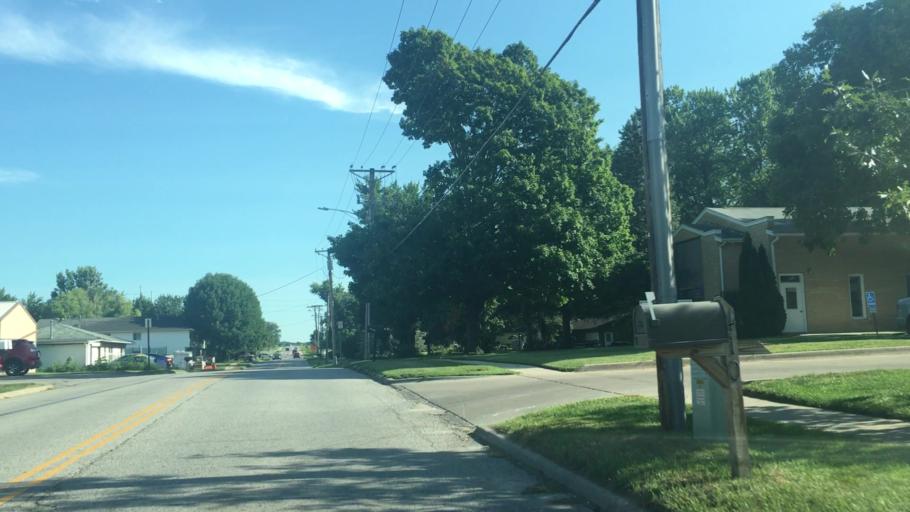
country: US
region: Iowa
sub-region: Johnson County
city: North Liberty
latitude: 41.7495
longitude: -91.5980
